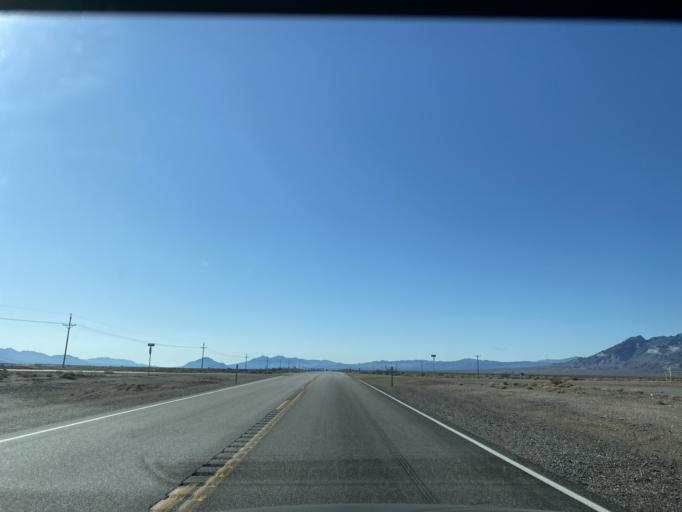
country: US
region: Nevada
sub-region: Nye County
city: Pahrump
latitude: 36.4490
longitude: -116.4219
